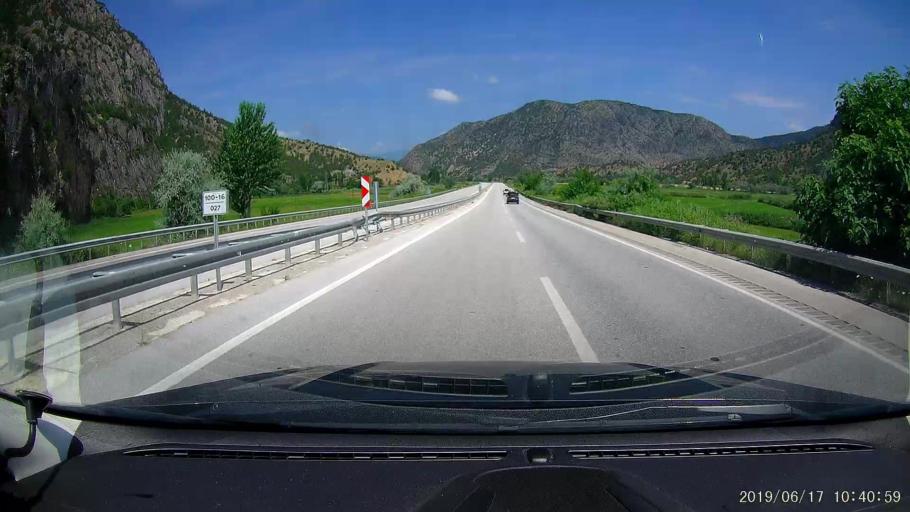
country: TR
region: Corum
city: Kargi
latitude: 41.0330
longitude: 34.5855
